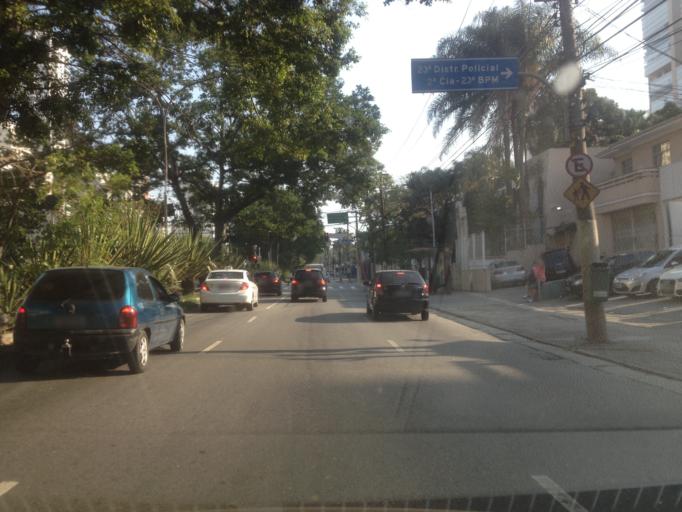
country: BR
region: Sao Paulo
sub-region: Sao Paulo
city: Sao Paulo
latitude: -23.5334
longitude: -46.6617
